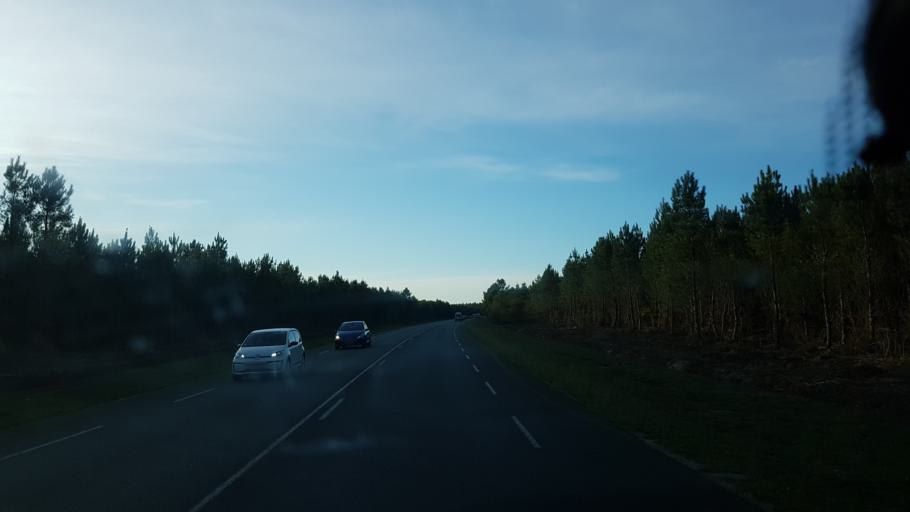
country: FR
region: Aquitaine
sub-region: Departement de la Gironde
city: Martignas-sur-Jalle
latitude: 44.8314
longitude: -0.7935
